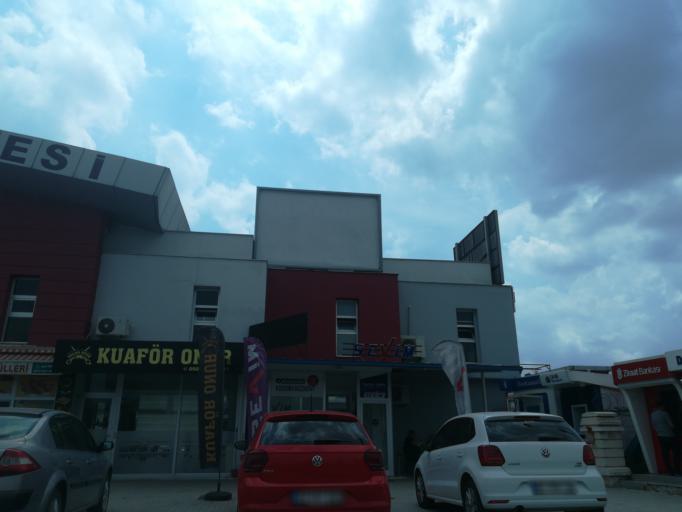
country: TR
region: Adana
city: Seyhan
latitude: 37.0026
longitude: 35.2451
